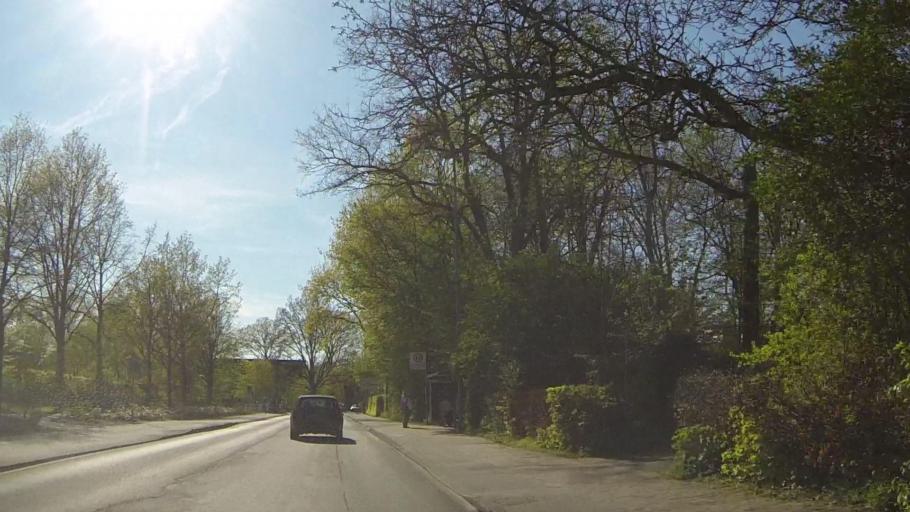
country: DE
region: Schleswig-Holstein
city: Rellingen
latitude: 53.6448
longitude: 9.7960
